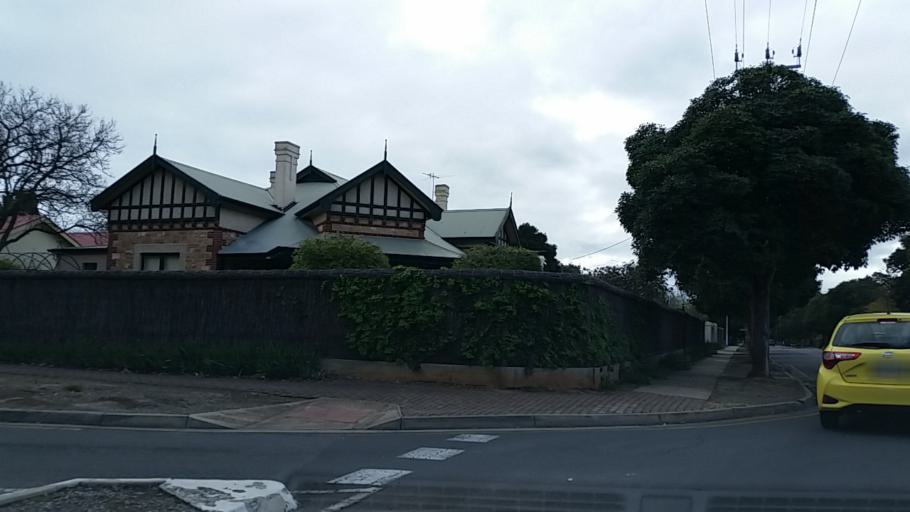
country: AU
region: South Australia
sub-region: Norwood Payneham St Peters
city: Royston Park
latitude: -34.9008
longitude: 138.6319
